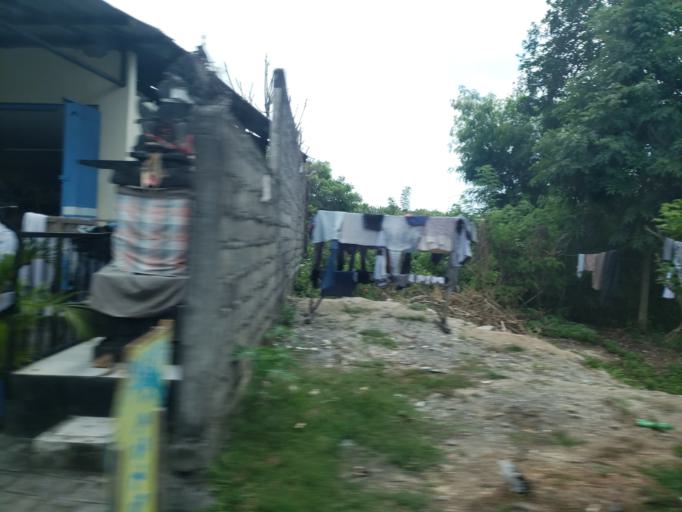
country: ID
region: Bali
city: Kangin
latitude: -8.8315
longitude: 115.1495
